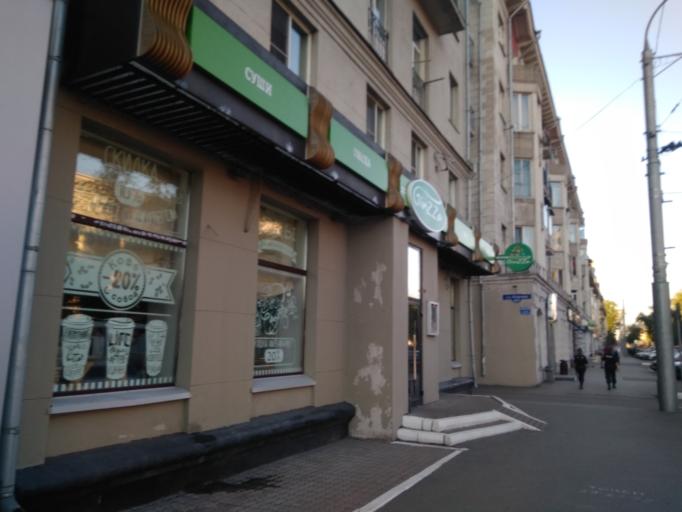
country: RU
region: Kemerovo
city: Novokuznetsk
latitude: 53.7578
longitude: 87.1198
